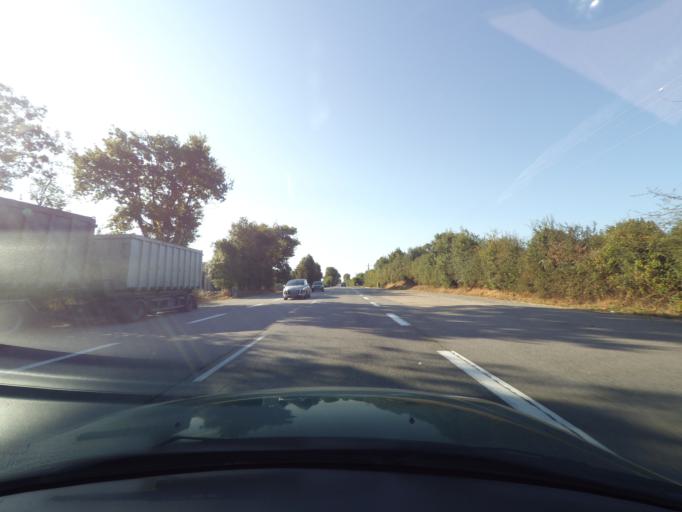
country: FR
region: Poitou-Charentes
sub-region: Departement des Deux-Sevres
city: Viennay
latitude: 46.6966
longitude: -0.2773
